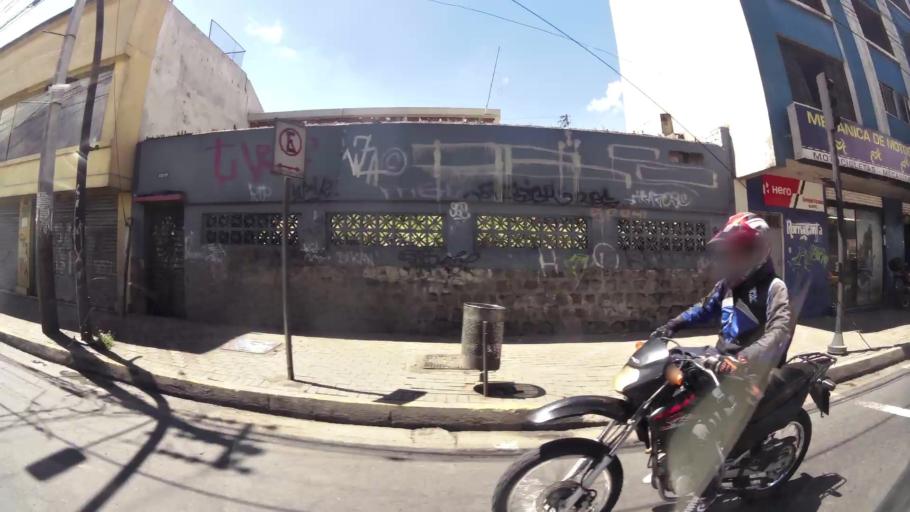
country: EC
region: Pichincha
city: Quito
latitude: -0.2601
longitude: -78.5227
